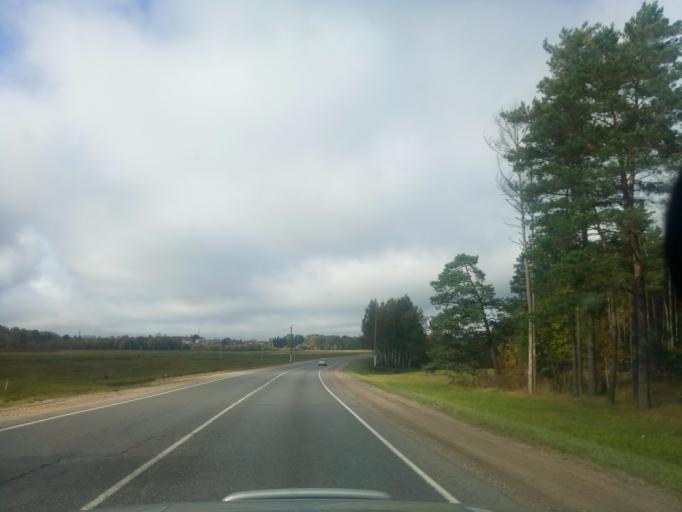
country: BY
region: Minsk
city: Zaslawye
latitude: 53.9931
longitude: 27.2968
